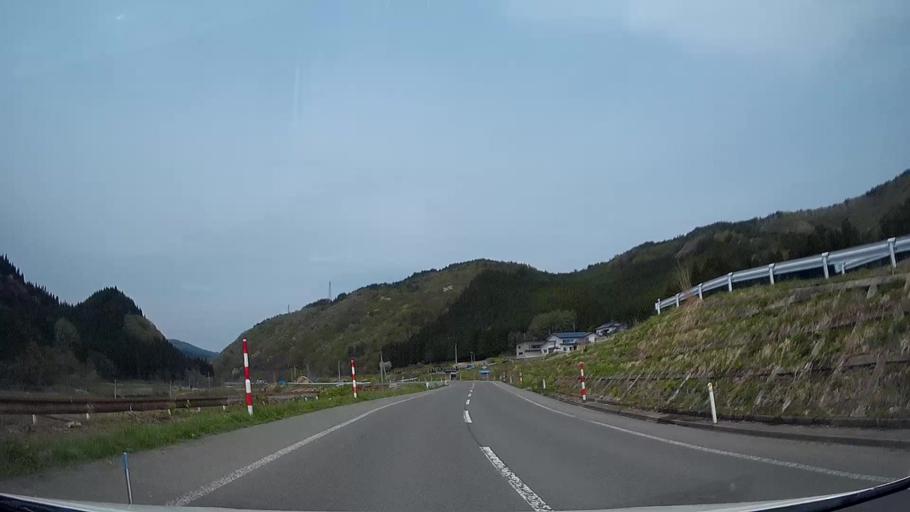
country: JP
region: Akita
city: Hanawa
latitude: 40.0710
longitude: 140.8012
